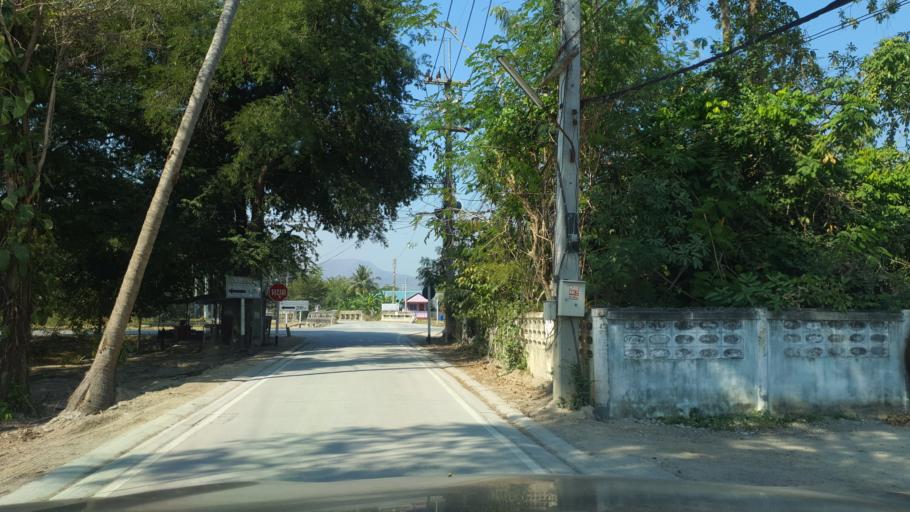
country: TH
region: Phetchaburi
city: Cha-am
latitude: 12.8295
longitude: 99.9308
